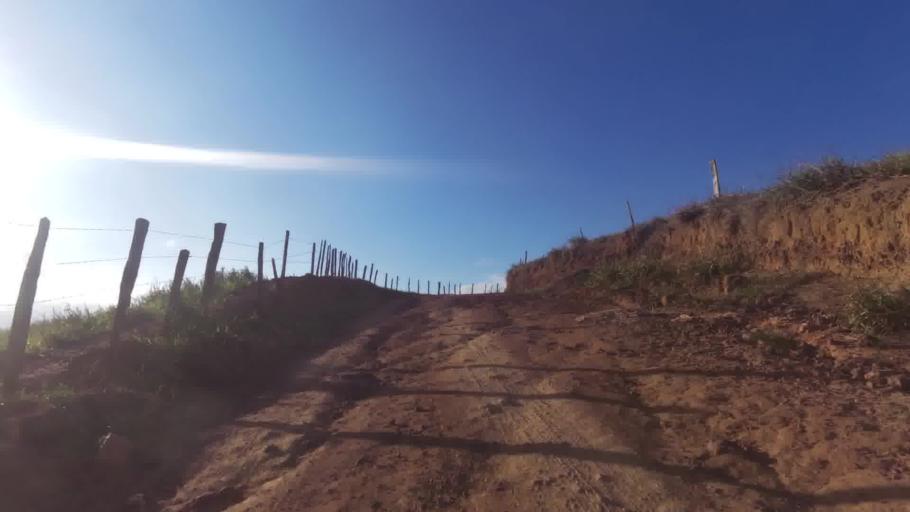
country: BR
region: Espirito Santo
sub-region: Marataizes
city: Marataizes
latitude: -21.1561
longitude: -41.0357
